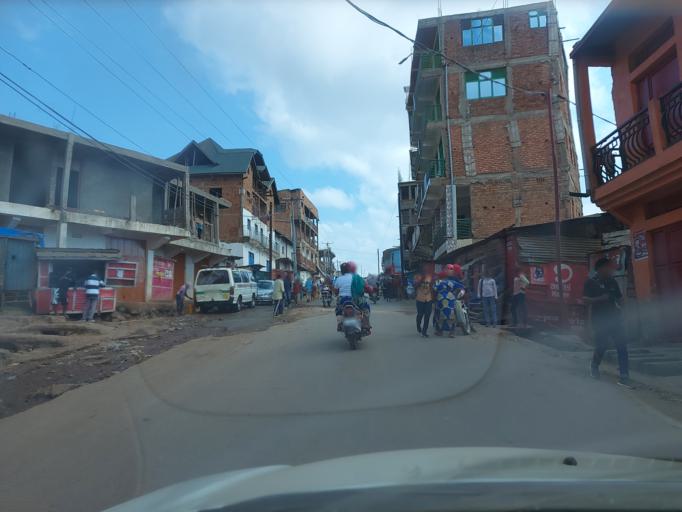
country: CD
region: South Kivu
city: Bukavu
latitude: -2.5213
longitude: 28.8520
